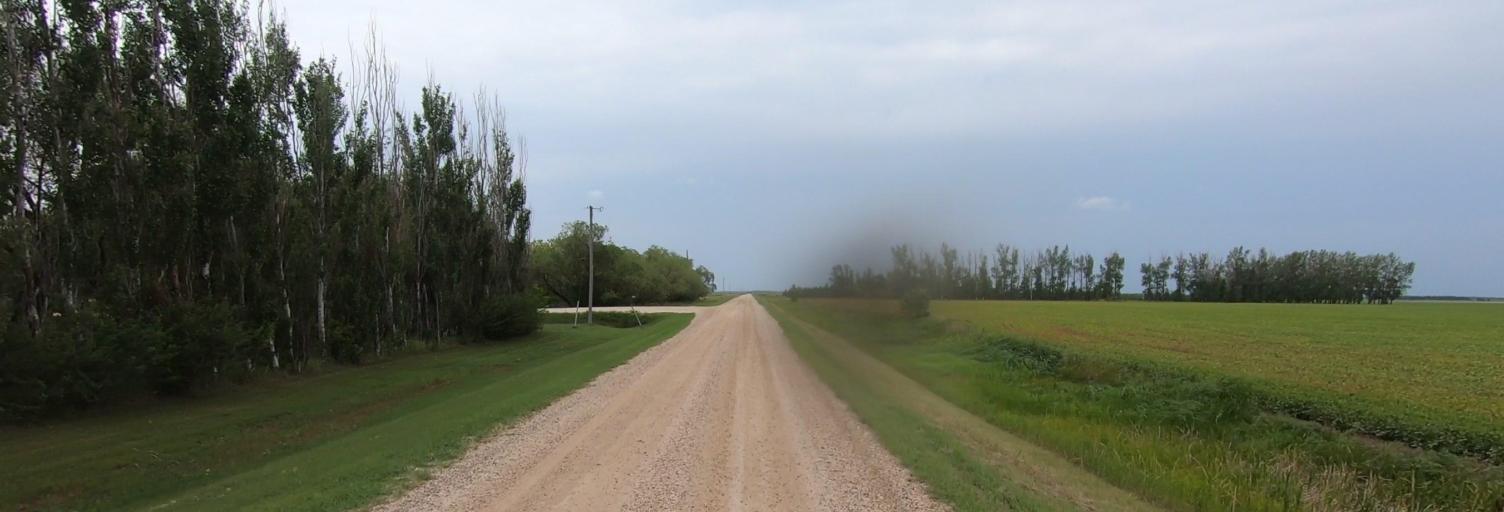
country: CA
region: Manitoba
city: Headingley
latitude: 49.7349
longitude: -97.4136
